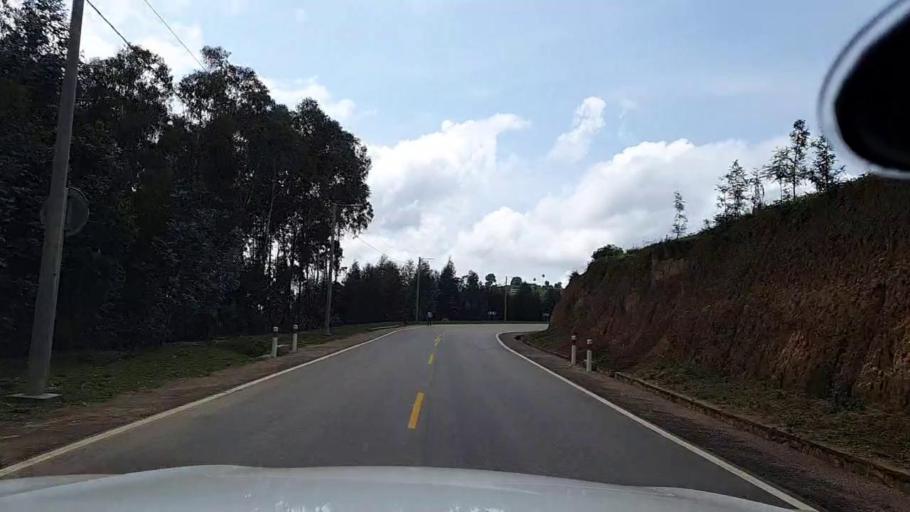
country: RW
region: Southern Province
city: Nzega
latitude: -2.5230
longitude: 29.4541
